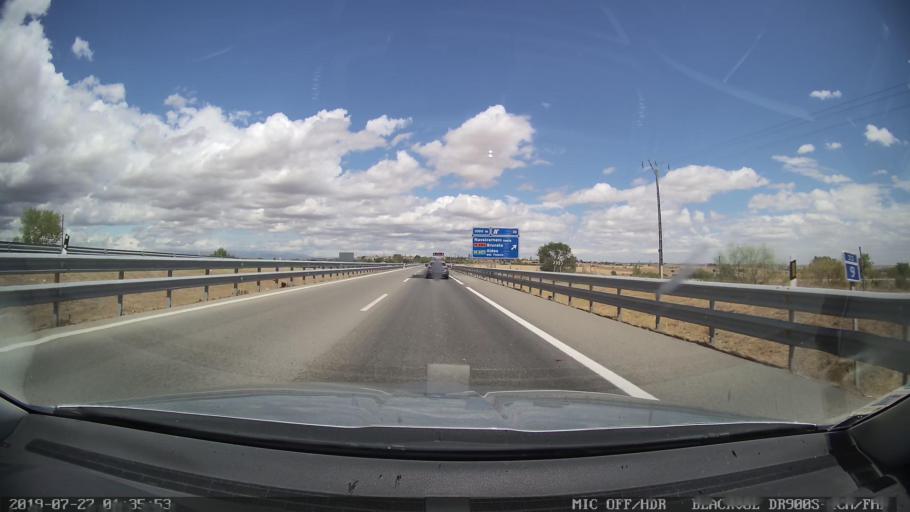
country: ES
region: Madrid
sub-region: Provincia de Madrid
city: Navalcarnero
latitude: 40.2717
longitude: -4.0335
